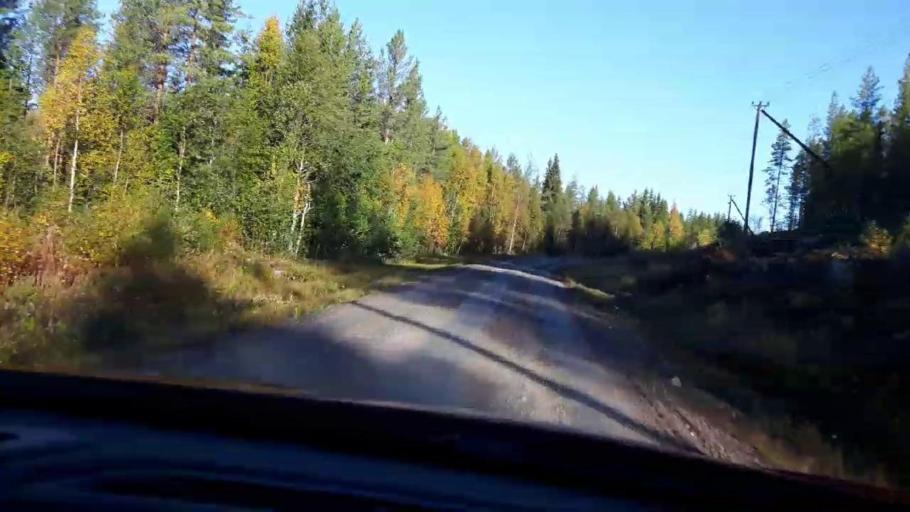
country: SE
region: Jaemtland
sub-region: Stroemsunds Kommun
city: Stroemsund
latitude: 64.3735
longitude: 15.1529
